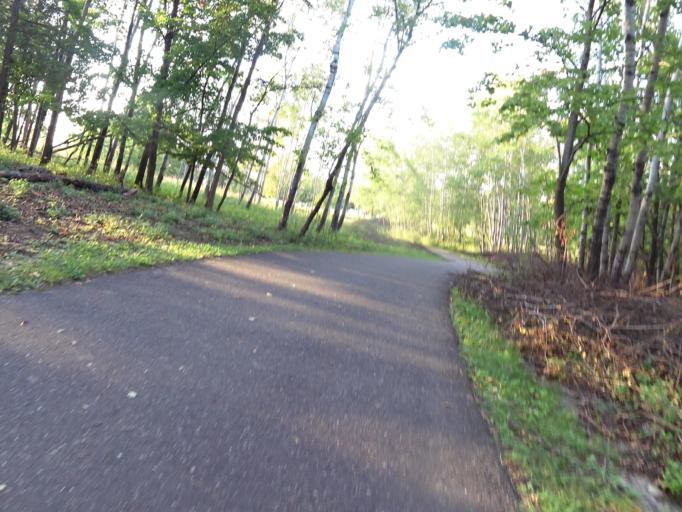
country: US
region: Minnesota
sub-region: Washington County
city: Afton
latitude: 44.8538
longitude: -92.7739
